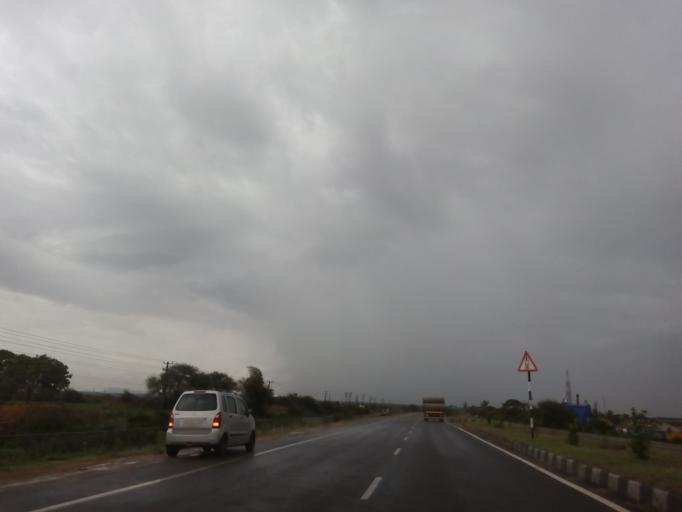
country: IN
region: Karnataka
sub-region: Davanagere
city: Harihar
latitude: 14.4308
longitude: 75.9328
